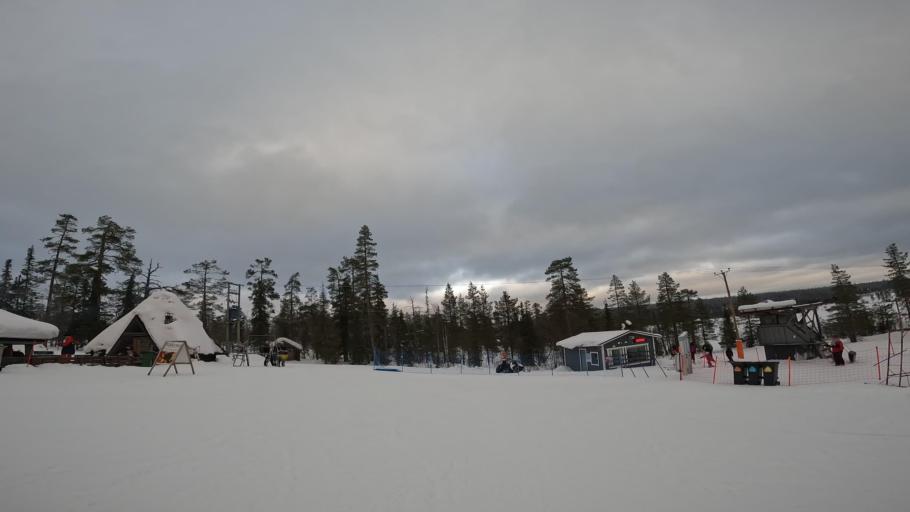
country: FI
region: Lapland
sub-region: Itae-Lappi
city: Salla
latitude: 66.7664
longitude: 28.7993
